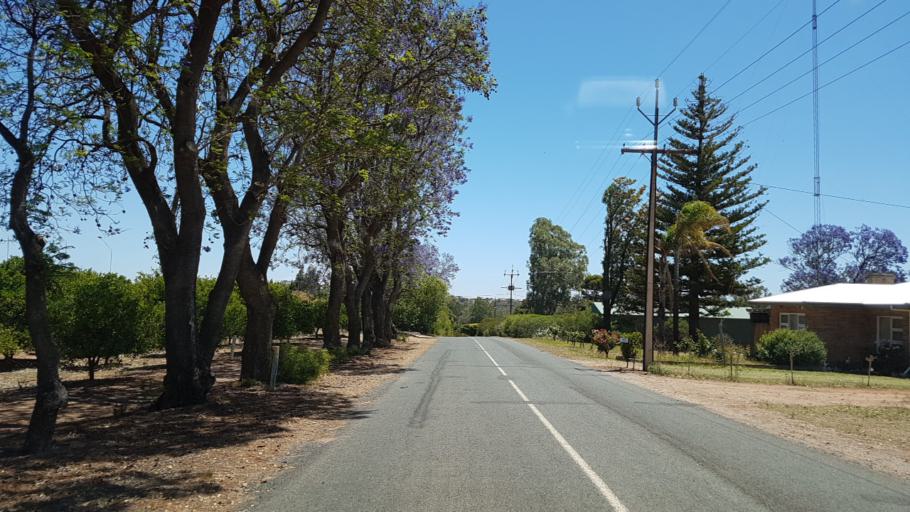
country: AU
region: South Australia
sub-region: Loxton Waikerie
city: Waikerie
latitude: -34.1667
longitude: 140.0360
